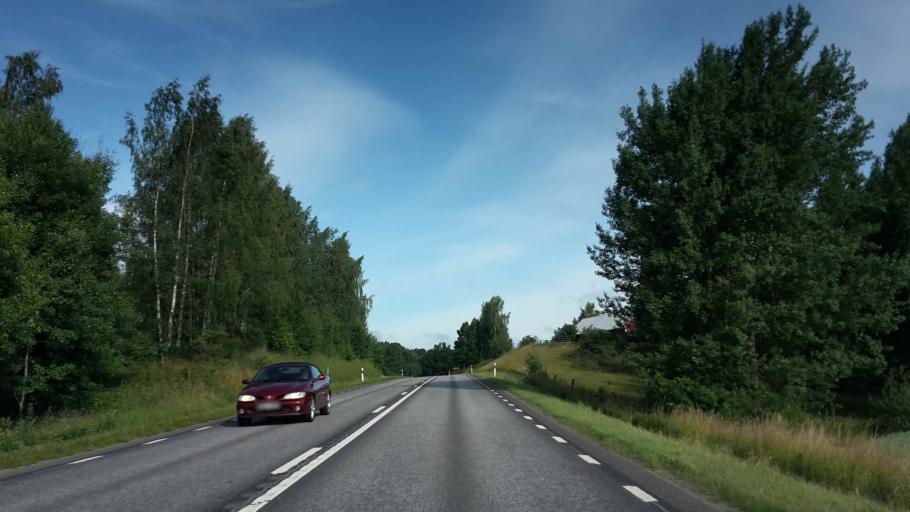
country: SE
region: OEstergoetland
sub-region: Motala Kommun
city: Borensberg
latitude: 58.5353
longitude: 15.3851
